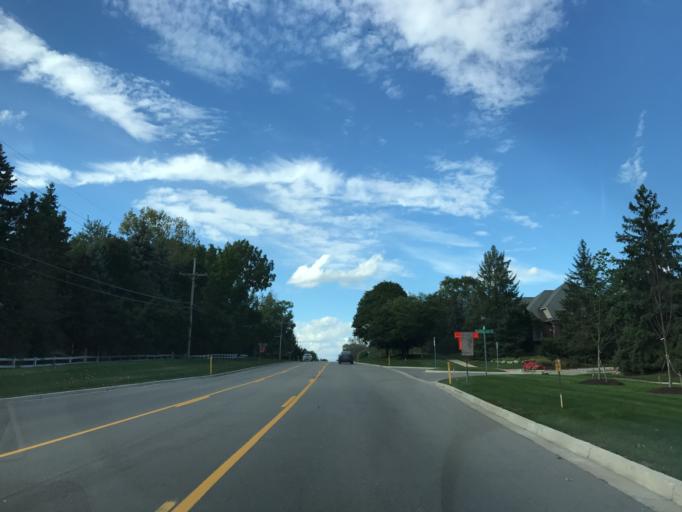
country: US
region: Michigan
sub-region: Oakland County
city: Farmington Hills
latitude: 42.5185
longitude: -83.3989
